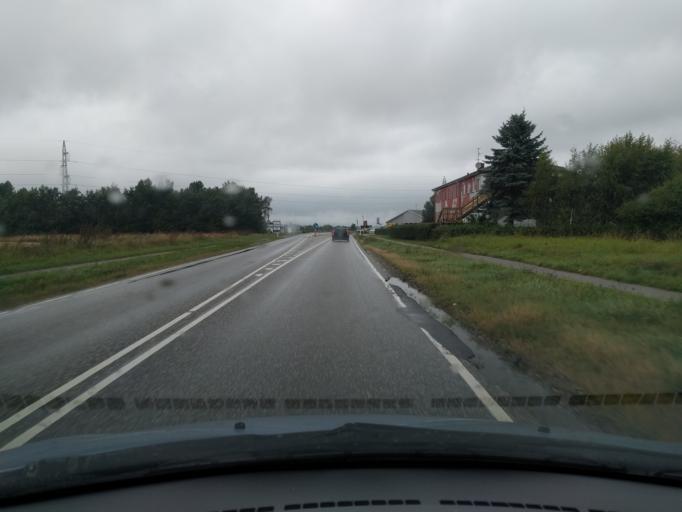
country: DK
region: Zealand
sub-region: Vordingborg Kommune
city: Neder Vindinge
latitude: 55.1117
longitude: 11.8196
